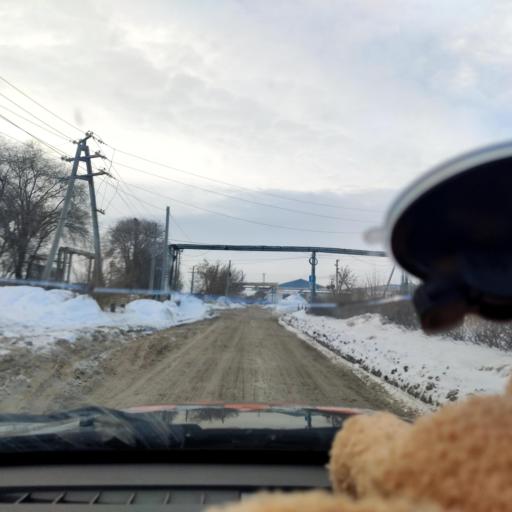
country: RU
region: Samara
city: Tol'yatti
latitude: 53.5770
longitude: 49.2841
